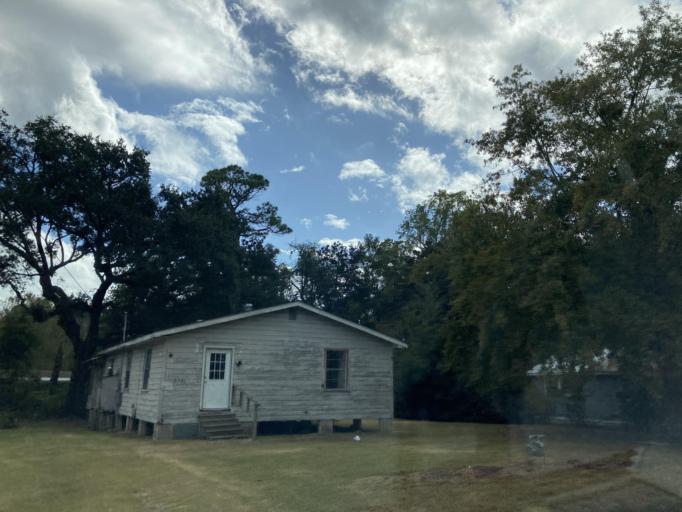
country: US
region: Mississippi
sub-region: Jackson County
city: Gulf Hills
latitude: 30.4343
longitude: -88.8312
